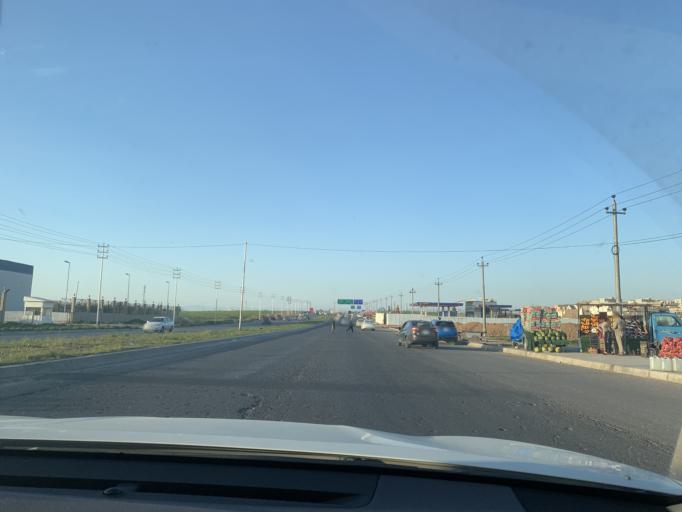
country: IQ
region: Arbil
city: Erbil
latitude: 36.2816
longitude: 44.0159
